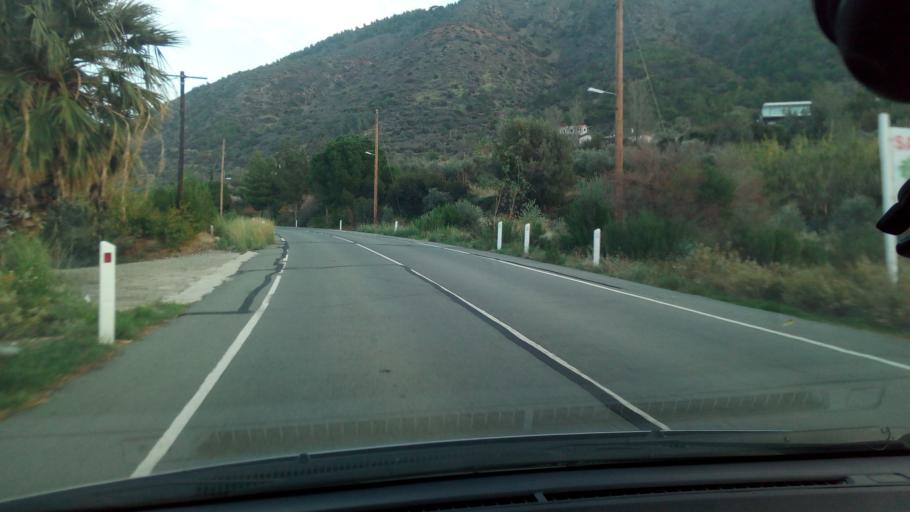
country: CY
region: Lefkosia
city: Kato Pyrgos
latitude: 35.1685
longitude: 32.5630
